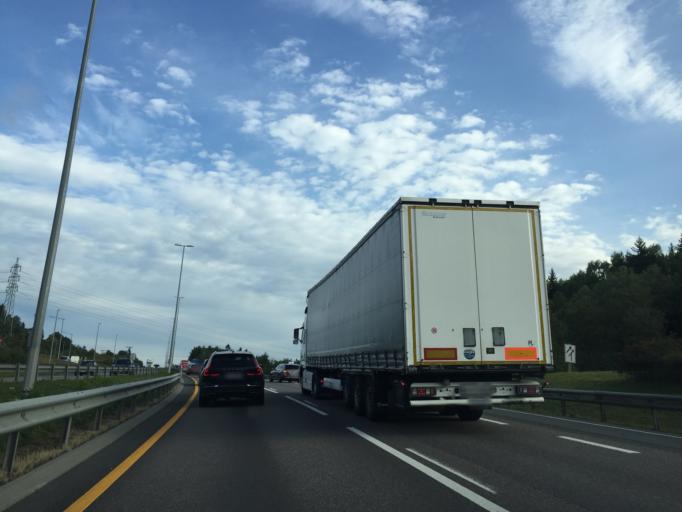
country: NO
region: Akershus
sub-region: Oppegard
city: Kolbotn
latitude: 59.8392
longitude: 10.8399
